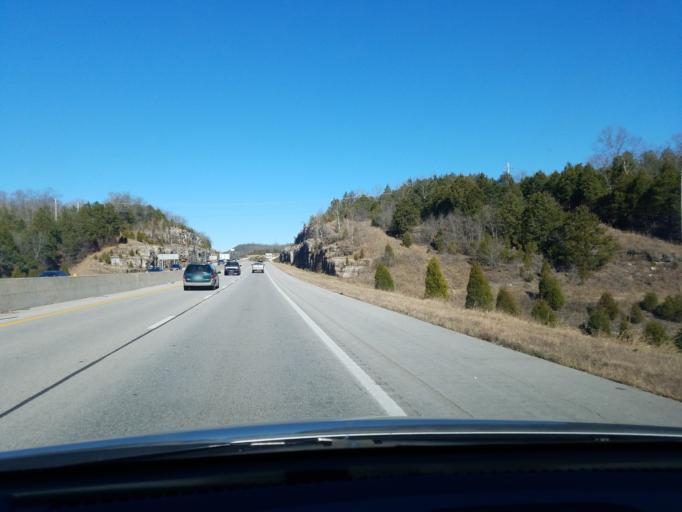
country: US
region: Missouri
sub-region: Taney County
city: Merriam Woods
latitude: 36.7272
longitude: -93.2206
